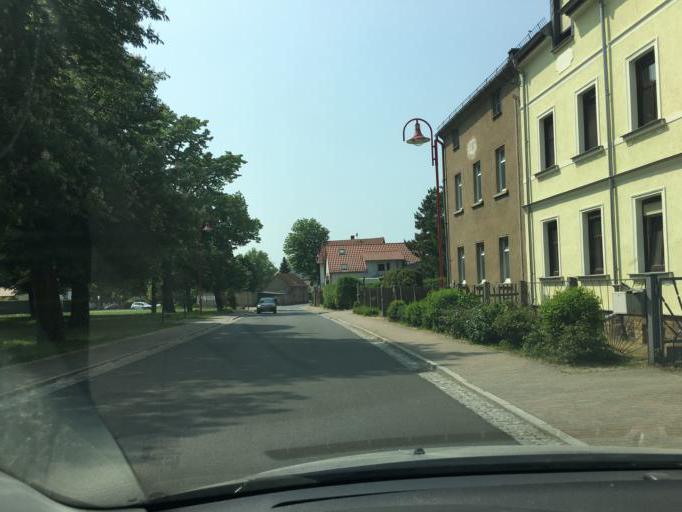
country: DE
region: Saxony
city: Grossposna
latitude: 51.2726
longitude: 12.5001
